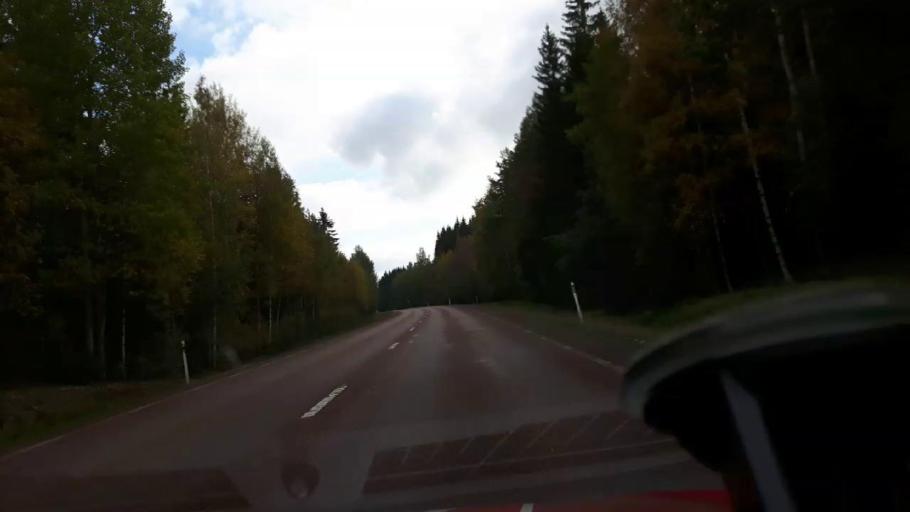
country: SE
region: Gaevleborg
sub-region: Ljusdals Kommun
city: Jaervsoe
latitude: 61.6396
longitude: 16.2368
